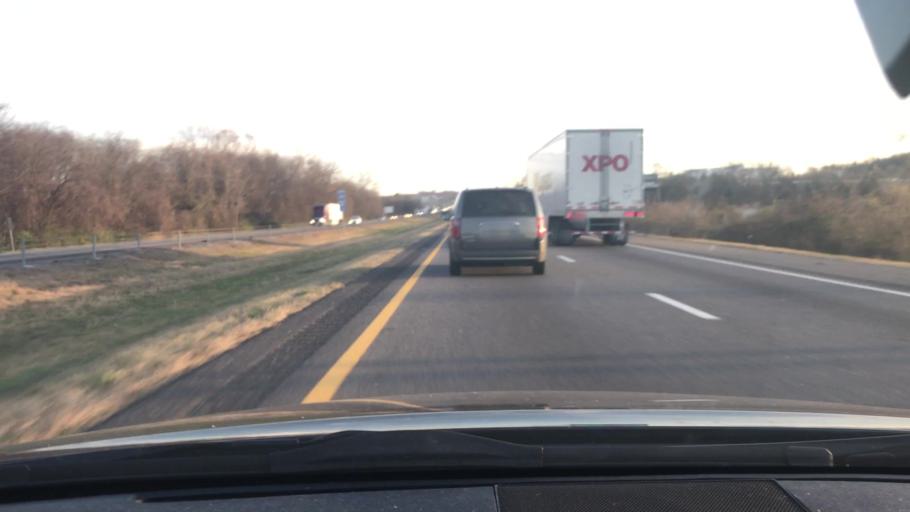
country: US
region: Tennessee
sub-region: Davidson County
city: Goodlettsville
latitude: 36.3389
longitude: -86.7126
